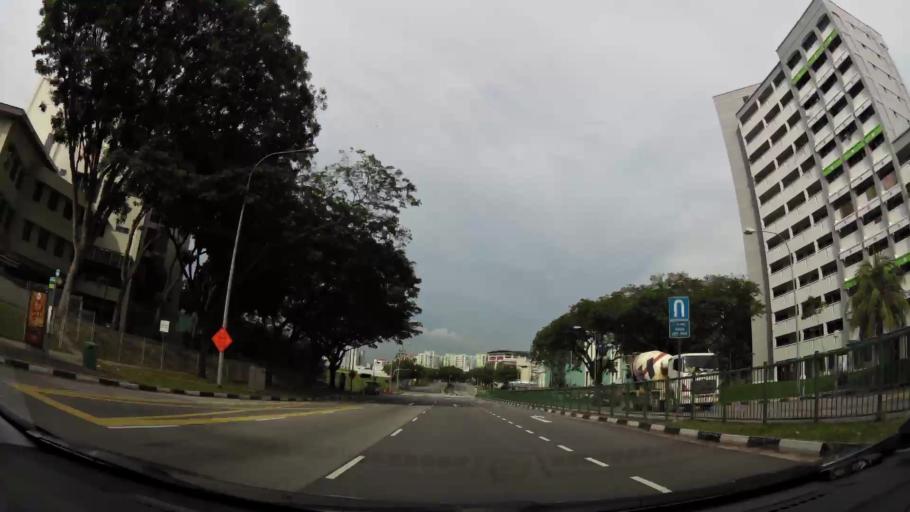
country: MY
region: Johor
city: Kampung Pasir Gudang Baru
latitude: 1.3816
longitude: 103.8881
